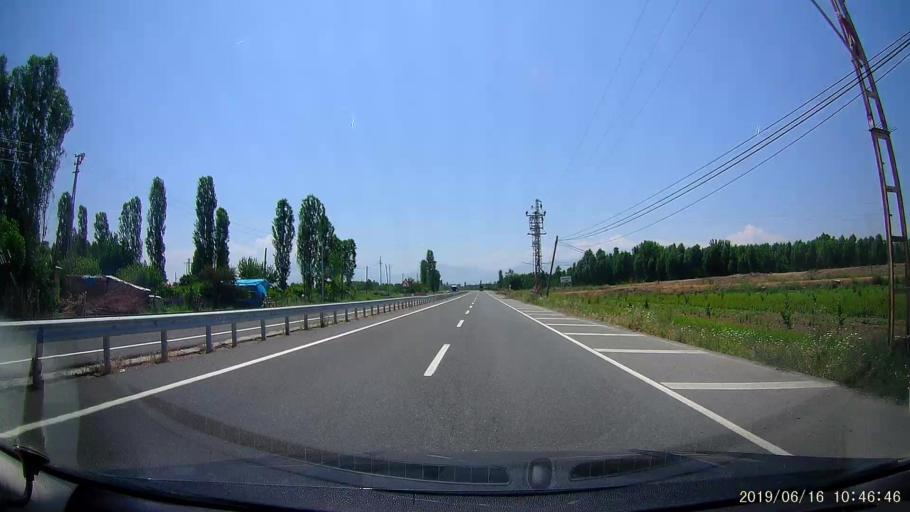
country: AM
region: Armavir
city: Shenavan
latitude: 40.0182
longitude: 43.8816
